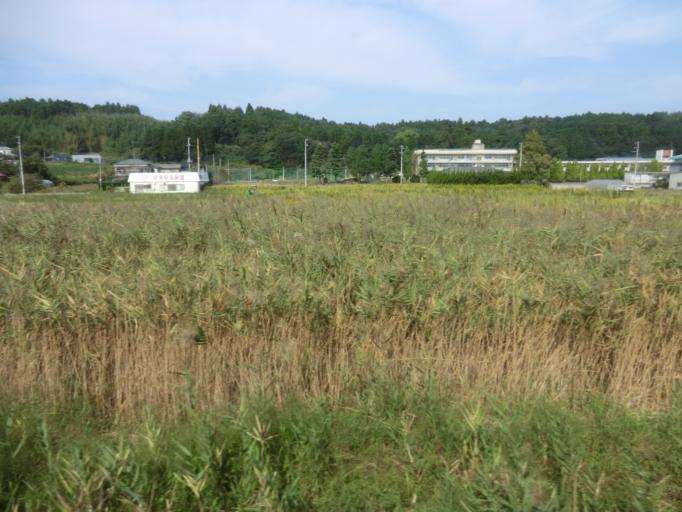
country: JP
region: Chiba
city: Naruto
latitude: 35.6086
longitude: 140.4054
